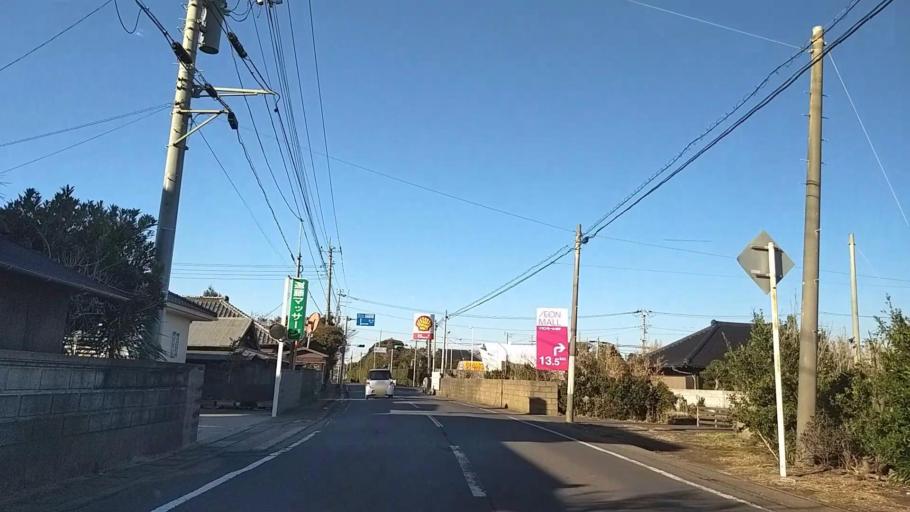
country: JP
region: Chiba
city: Asahi
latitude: 35.6935
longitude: 140.6615
